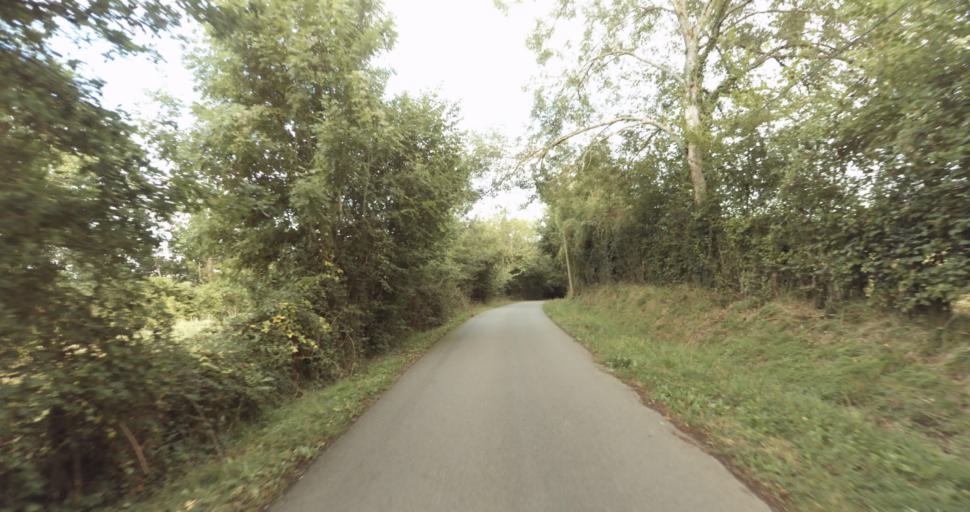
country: FR
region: Lower Normandy
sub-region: Departement de l'Orne
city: Vimoutiers
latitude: 48.8927
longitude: 0.2265
